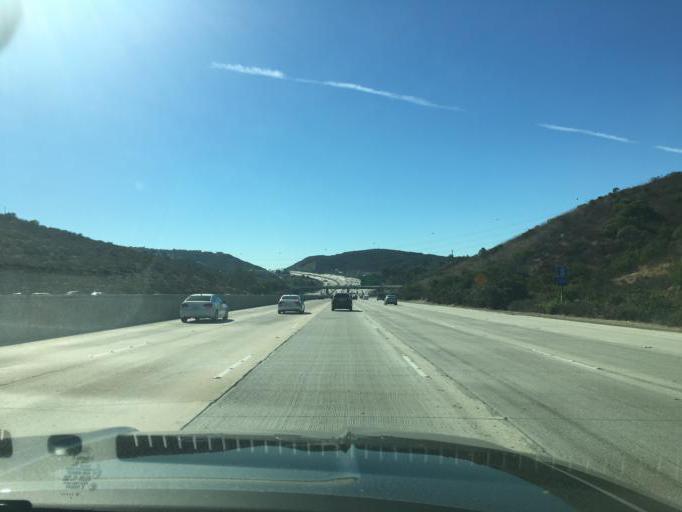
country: US
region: California
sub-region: San Diego County
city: Poway
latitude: 32.9542
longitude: -117.1023
